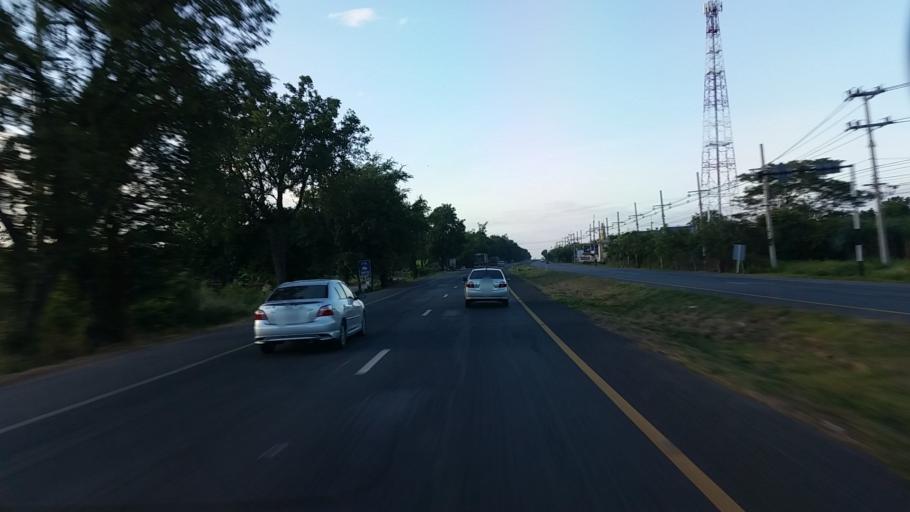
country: TH
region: Lop Buri
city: Chai Badan
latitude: 15.1662
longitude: 101.0628
